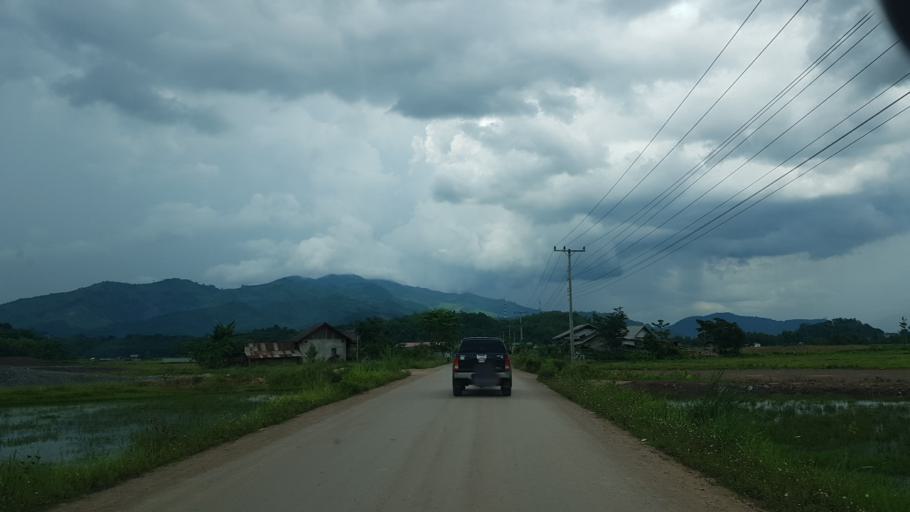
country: LA
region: Oudomxai
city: Muang Xay
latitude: 20.6772
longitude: 101.9702
